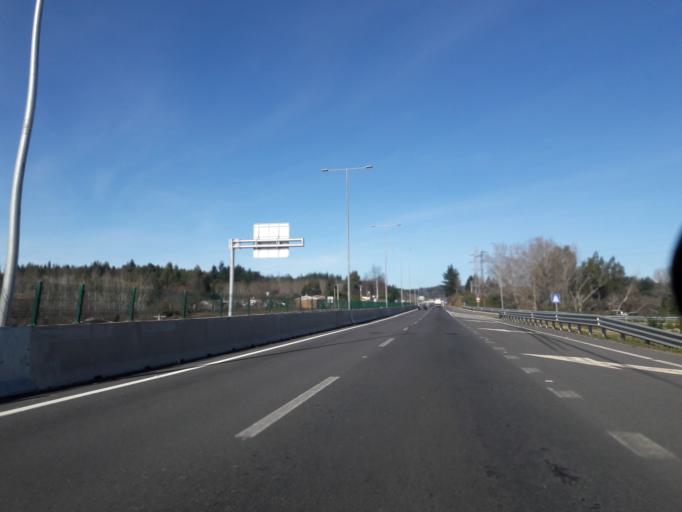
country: CL
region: Biobio
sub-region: Provincia de Concepcion
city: Chiguayante
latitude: -36.9090
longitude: -72.7786
